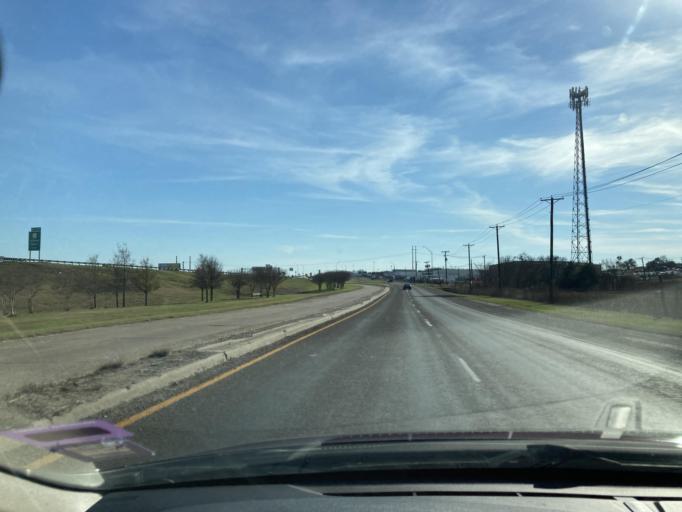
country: US
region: Texas
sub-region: Navarro County
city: Corsicana
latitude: 32.0661
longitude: -96.4531
